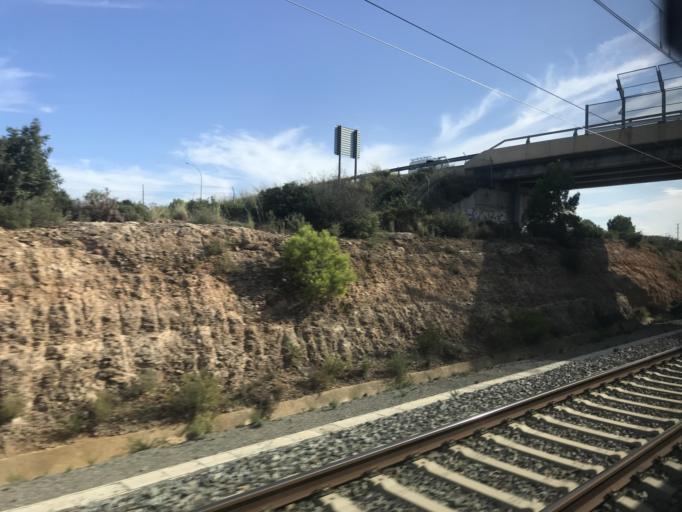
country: ES
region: Catalonia
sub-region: Provincia de Tarragona
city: Colldejou
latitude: 41.0235
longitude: 0.9321
